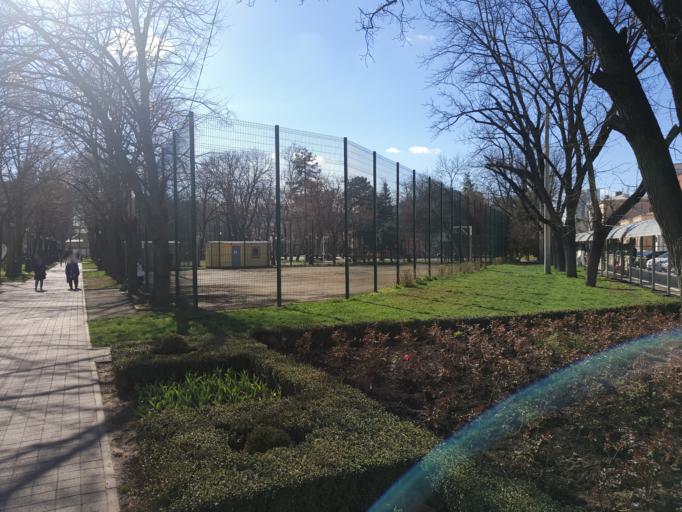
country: RU
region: Krasnodarskiy
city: Krasnodar
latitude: 45.0227
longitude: 38.9674
